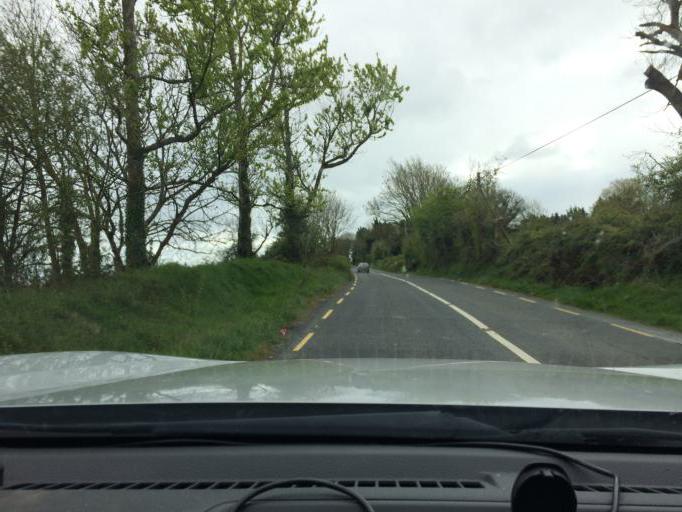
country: IE
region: Munster
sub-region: Waterford
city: Dungarvan
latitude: 52.0567
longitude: -7.6398
